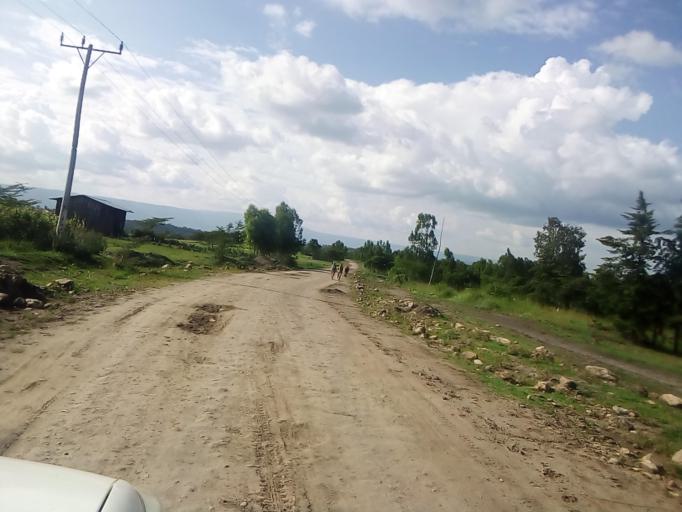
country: ET
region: Southern Nations, Nationalities, and People's Region
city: K'olito
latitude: 7.6434
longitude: 38.0532
